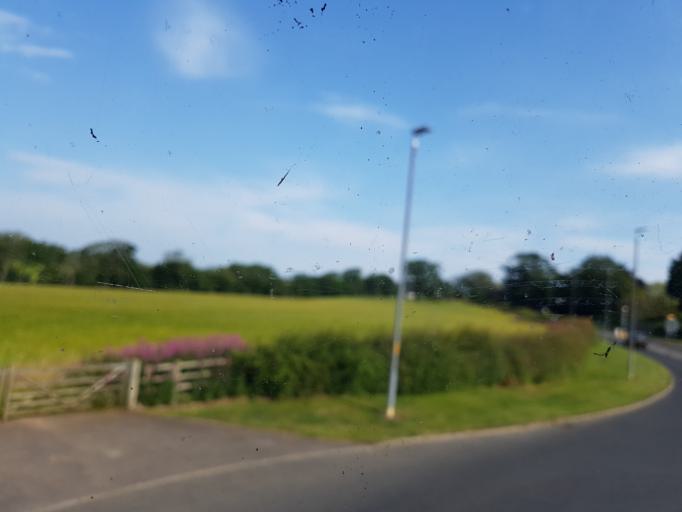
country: GB
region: England
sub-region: Northumberland
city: Alnmouth
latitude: 55.3980
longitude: -1.6352
